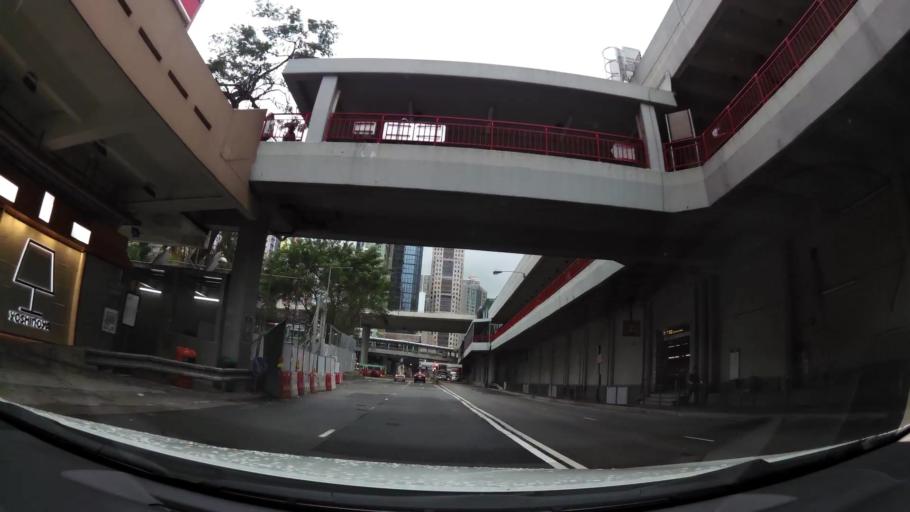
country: HK
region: Tsuen Wan
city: Tsuen Wan
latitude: 22.3734
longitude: 114.1185
